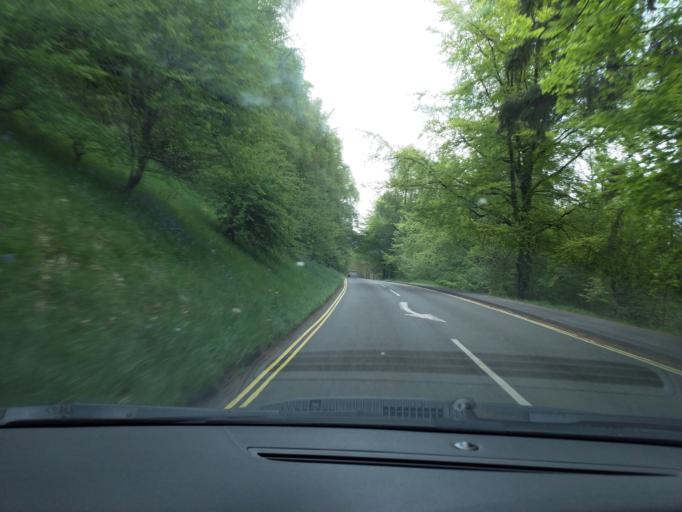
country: GB
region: England
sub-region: Derbyshire
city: Hope Valley
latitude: 53.3875
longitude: -1.7213
